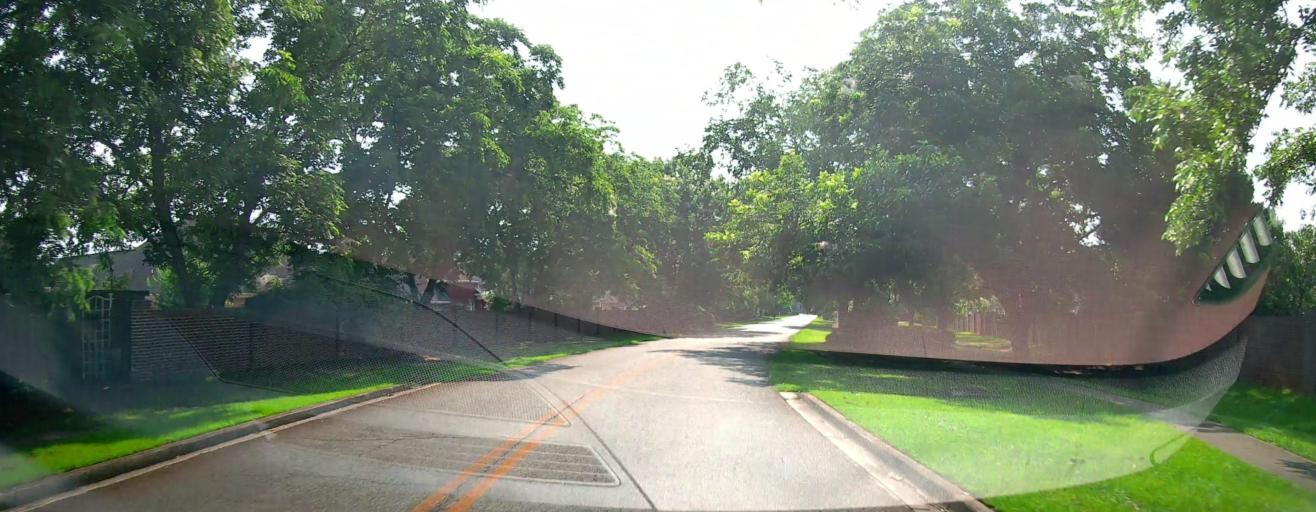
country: US
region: Georgia
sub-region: Houston County
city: Centerville
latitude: 32.6261
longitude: -83.6951
